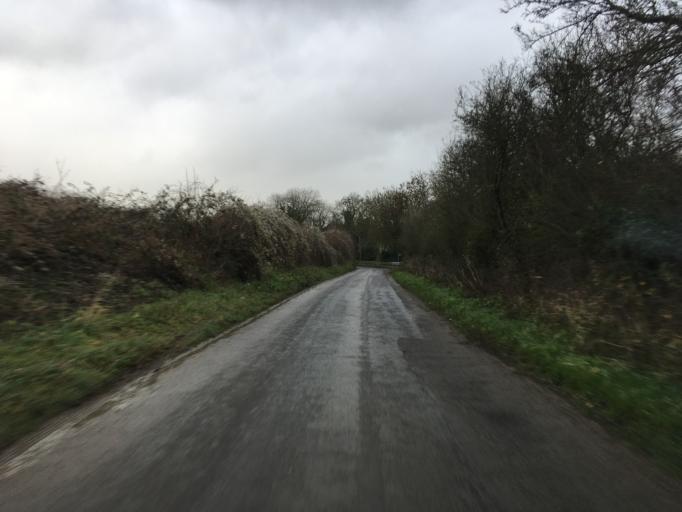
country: GB
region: England
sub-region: Wiltshire
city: Nettleton
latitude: 51.5130
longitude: -2.2759
